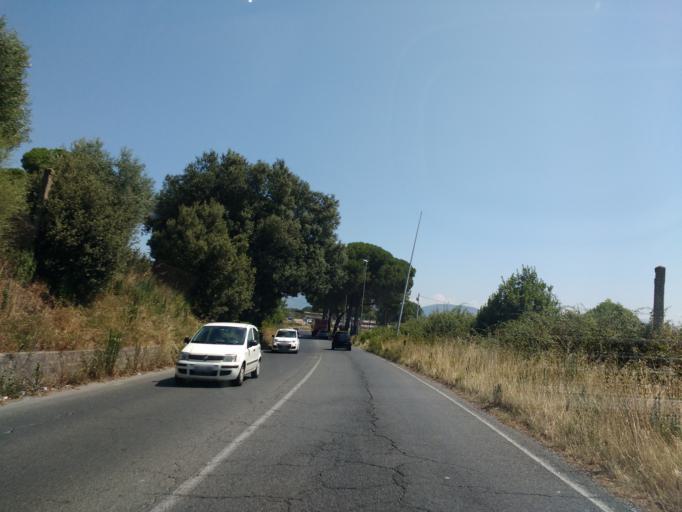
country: IT
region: Latium
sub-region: Citta metropolitana di Roma Capitale
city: Albuccione
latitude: 41.9505
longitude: 12.6851
